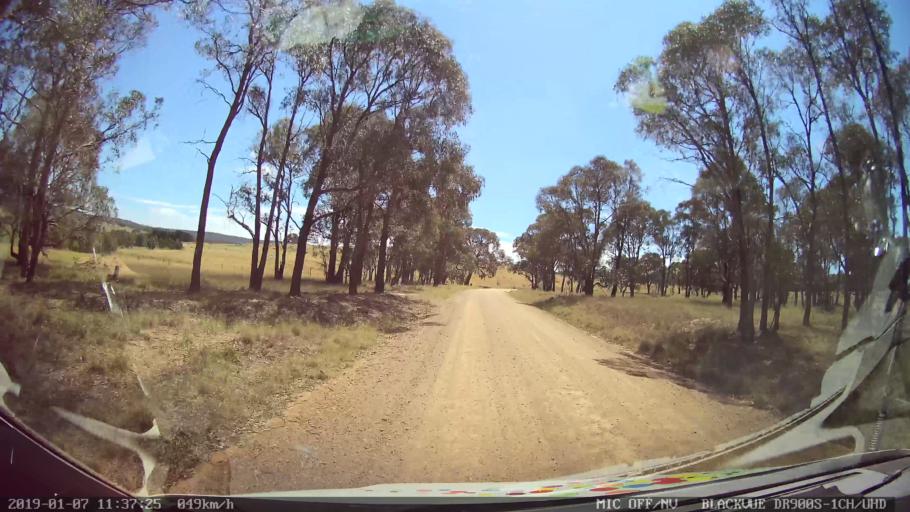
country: AU
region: New South Wales
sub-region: Armidale Dumaresq
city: Armidale
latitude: -30.3710
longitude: 151.5654
